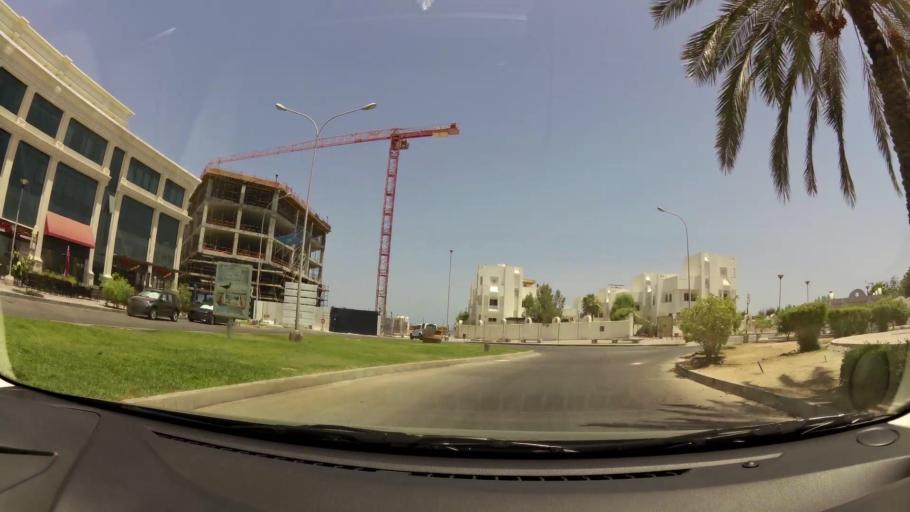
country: OM
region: Muhafazat Masqat
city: Bawshar
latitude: 23.6122
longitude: 58.4543
